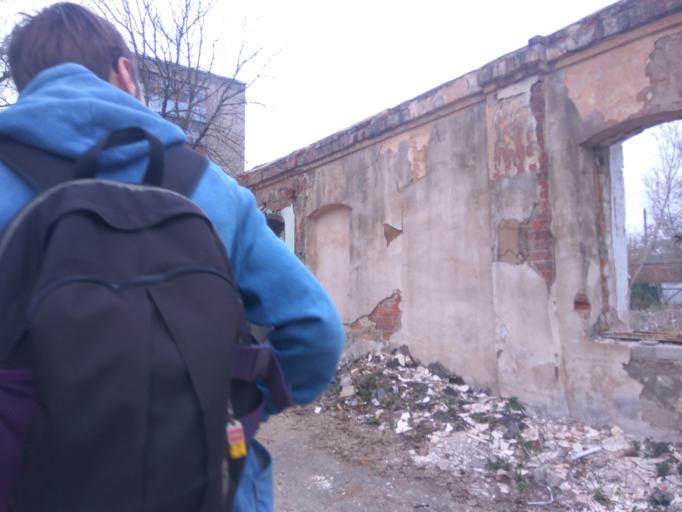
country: RU
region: Vladimir
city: Aleksandrov
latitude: 56.3979
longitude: 38.7224
